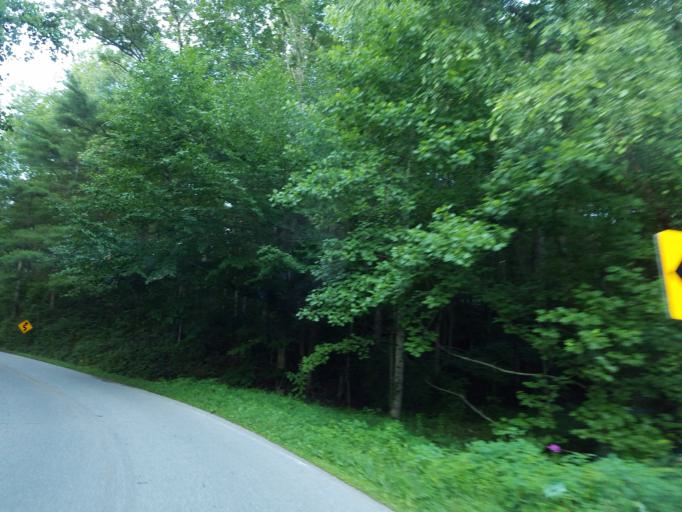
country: US
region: Georgia
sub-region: Lumpkin County
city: Dahlonega
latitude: 34.7022
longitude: -84.0537
